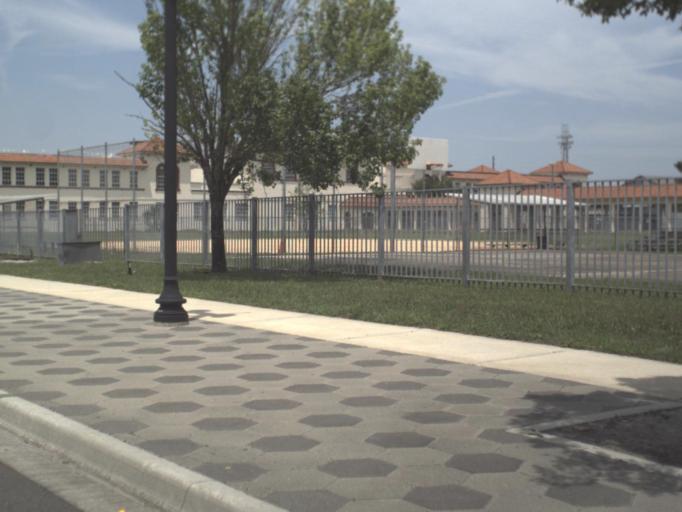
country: US
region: Florida
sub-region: Duval County
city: Jacksonville
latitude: 30.3495
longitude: -81.6536
